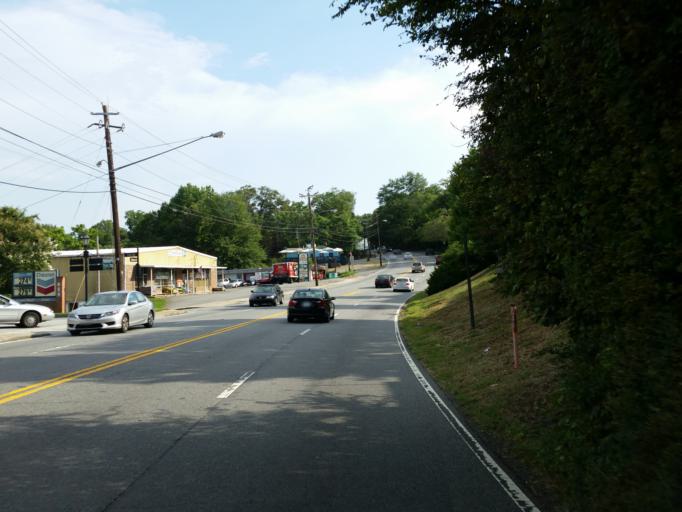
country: US
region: Georgia
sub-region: Fulton County
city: Roswell
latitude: 34.0182
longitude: -84.3620
